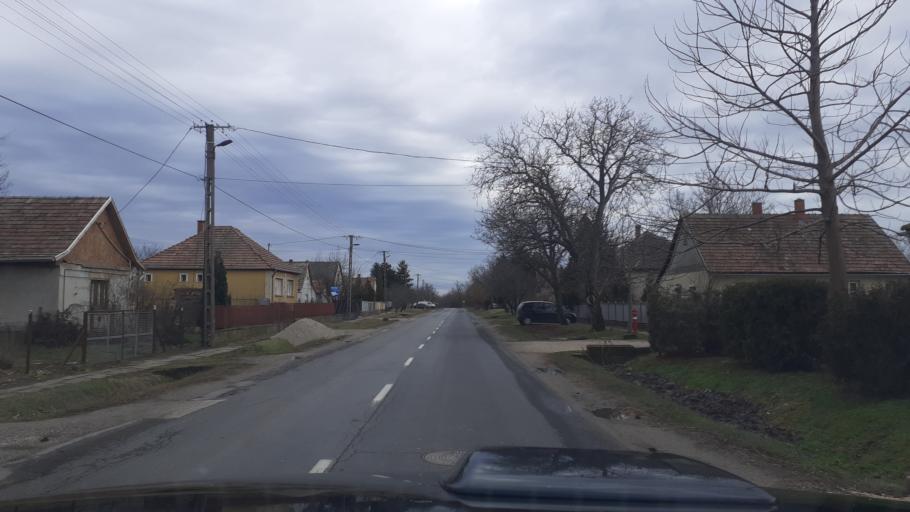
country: HU
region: Fejer
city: Sarosd
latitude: 47.0351
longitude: 18.6586
